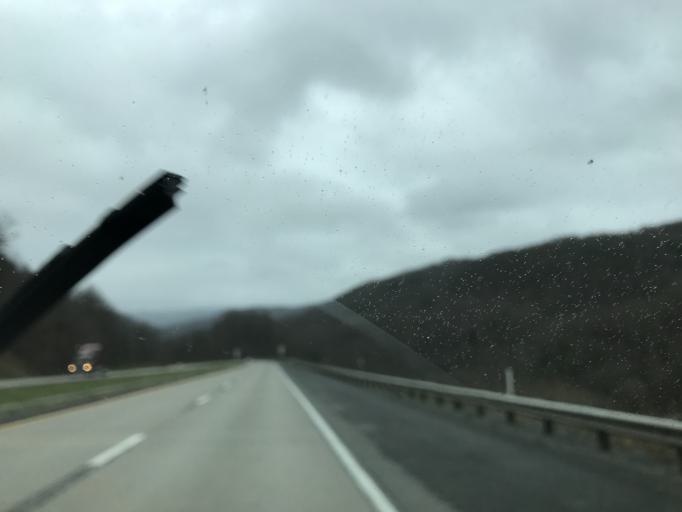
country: US
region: West Virginia
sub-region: Summers County
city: Hinton
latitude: 37.7814
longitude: -80.9558
